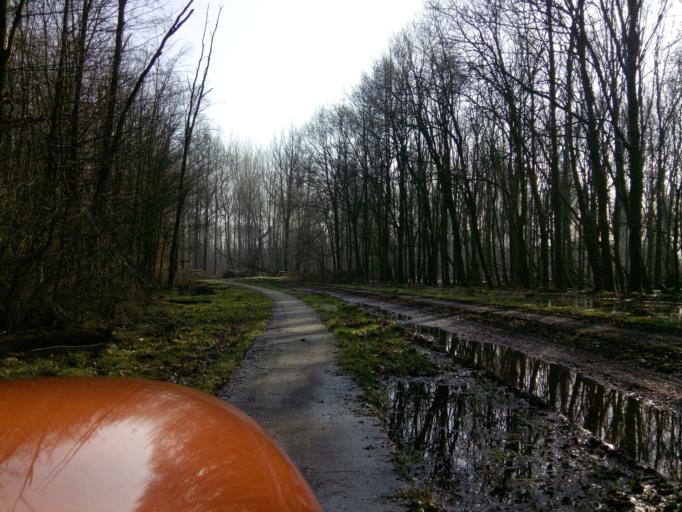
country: NL
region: Utrecht
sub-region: Gemeente Bunschoten
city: Bunschoten
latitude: 52.2594
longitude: 5.4170
